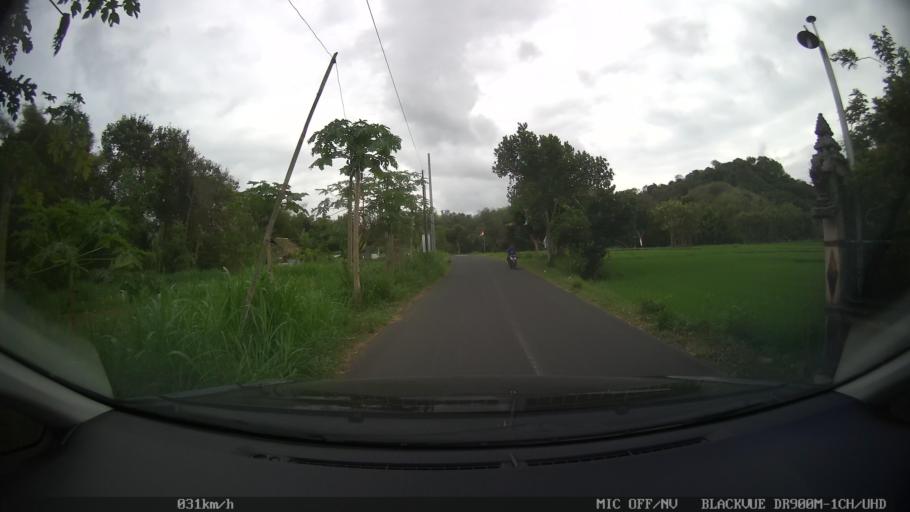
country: ID
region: Daerah Istimewa Yogyakarta
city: Sewon
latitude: -7.8686
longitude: 110.4192
